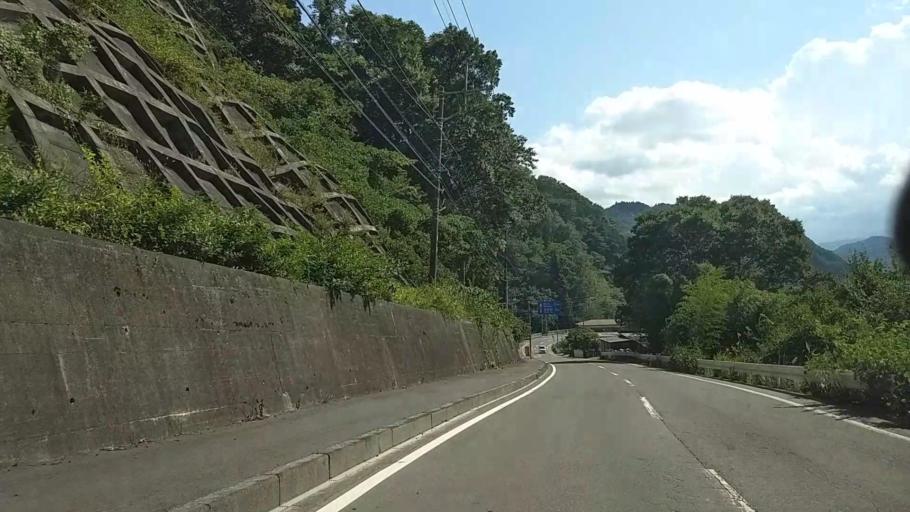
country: JP
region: Yamanashi
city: Ryuo
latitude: 35.4125
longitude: 138.4568
